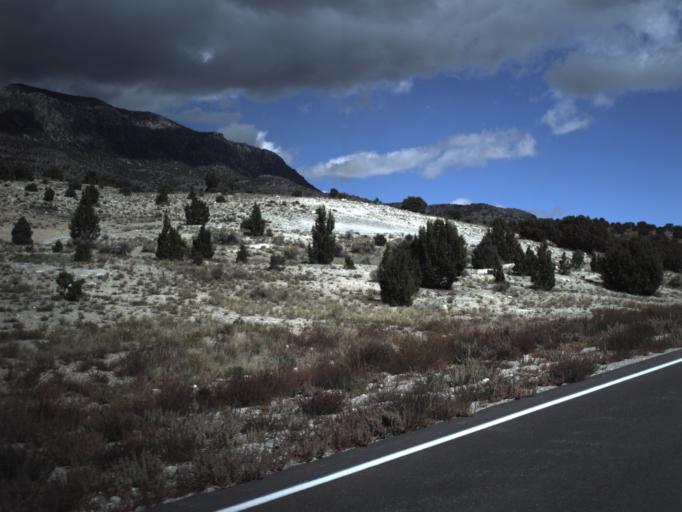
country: US
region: Utah
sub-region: Beaver County
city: Milford
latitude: 38.5155
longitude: -113.5593
